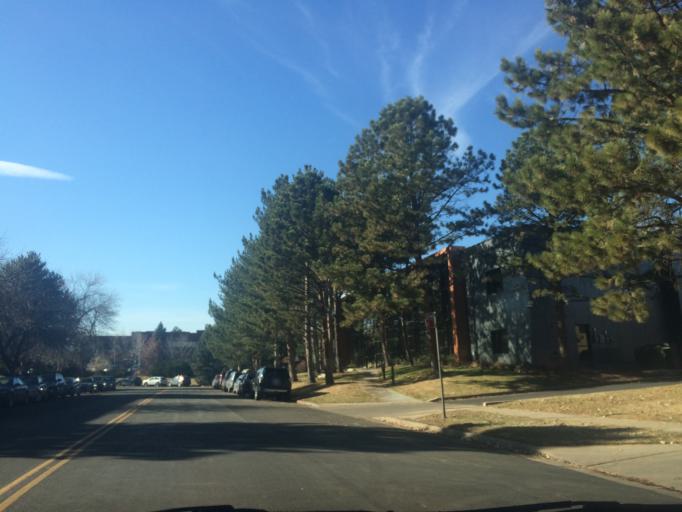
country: US
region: Colorado
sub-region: Boulder County
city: Boulder
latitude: 40.0255
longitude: -105.2196
